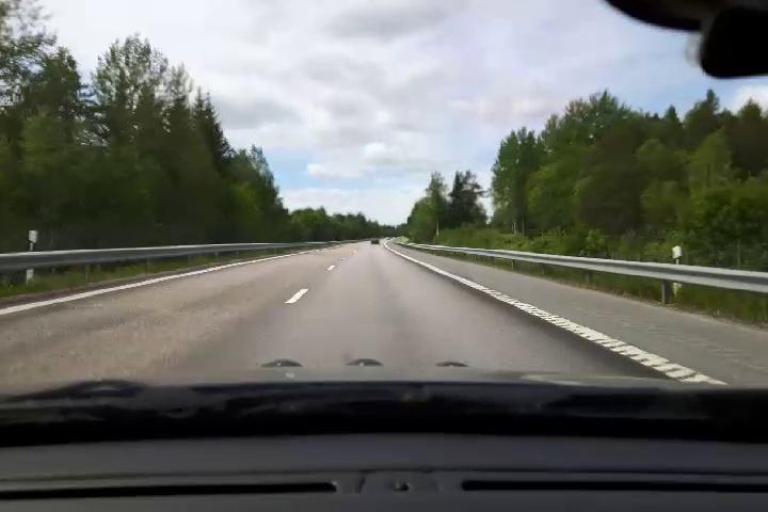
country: SE
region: Uppsala
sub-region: Alvkarleby Kommun
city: AElvkarleby
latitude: 60.4749
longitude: 17.3810
